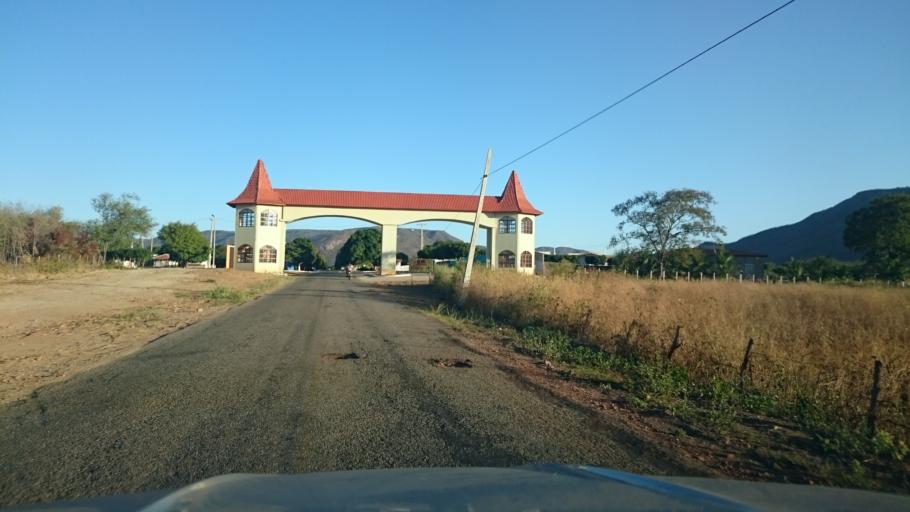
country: BR
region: Rio Grande do Norte
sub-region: Umarizal
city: Umarizal
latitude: -5.9881
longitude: -37.9488
